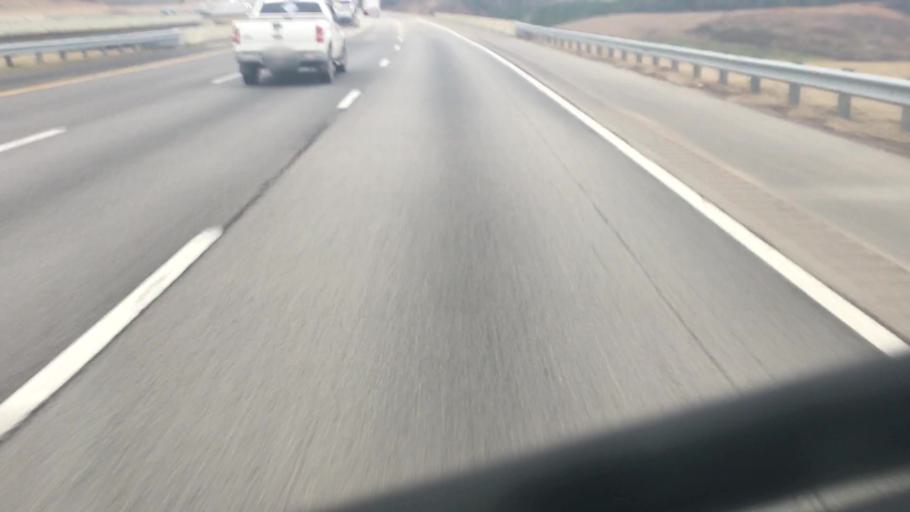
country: US
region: Alabama
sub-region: Walker County
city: Dora
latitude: 33.6789
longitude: -87.0828
